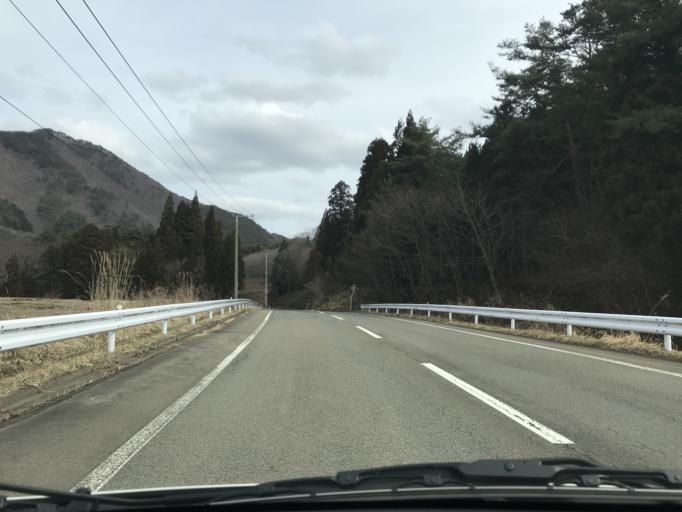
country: JP
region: Iwate
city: Tono
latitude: 39.2984
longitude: 141.3389
